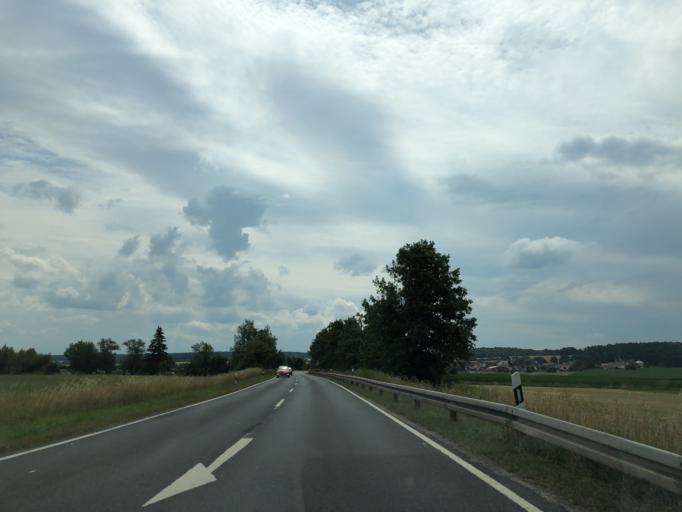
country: DE
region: Bavaria
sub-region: Regierungsbezirk Mittelfranken
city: Muhlhausen
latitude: 49.7504
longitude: 10.7708
